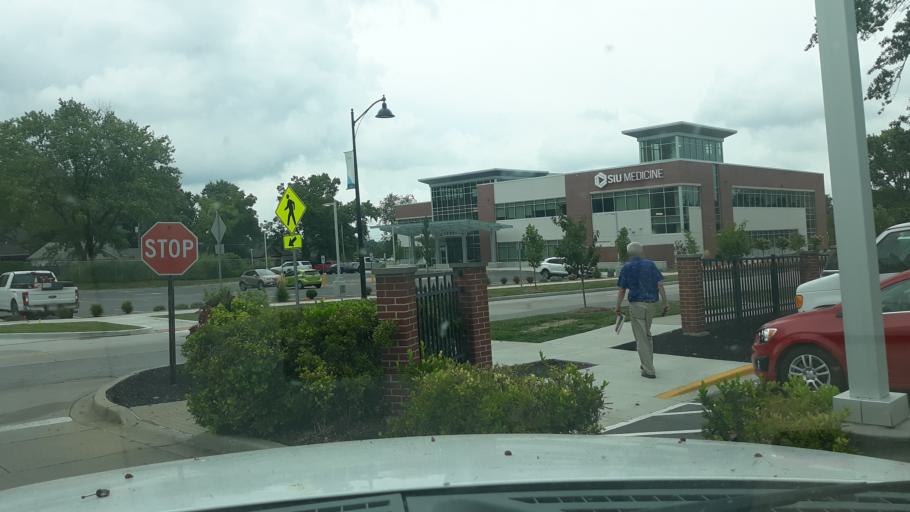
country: US
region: Illinois
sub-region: Jackson County
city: Carbondale
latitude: 37.7287
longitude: -89.2202
